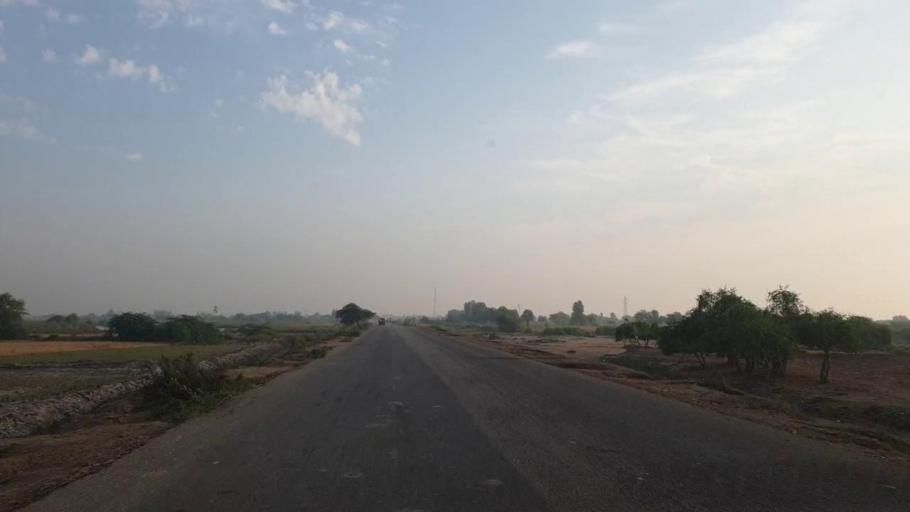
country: PK
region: Sindh
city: Badin
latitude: 24.6998
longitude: 68.9225
